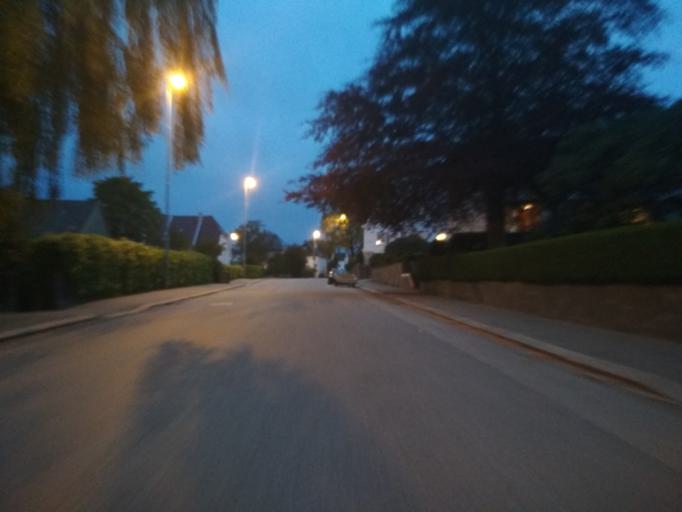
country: NO
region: Rogaland
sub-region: Stavanger
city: Stavanger
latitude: 58.9570
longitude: 5.7373
